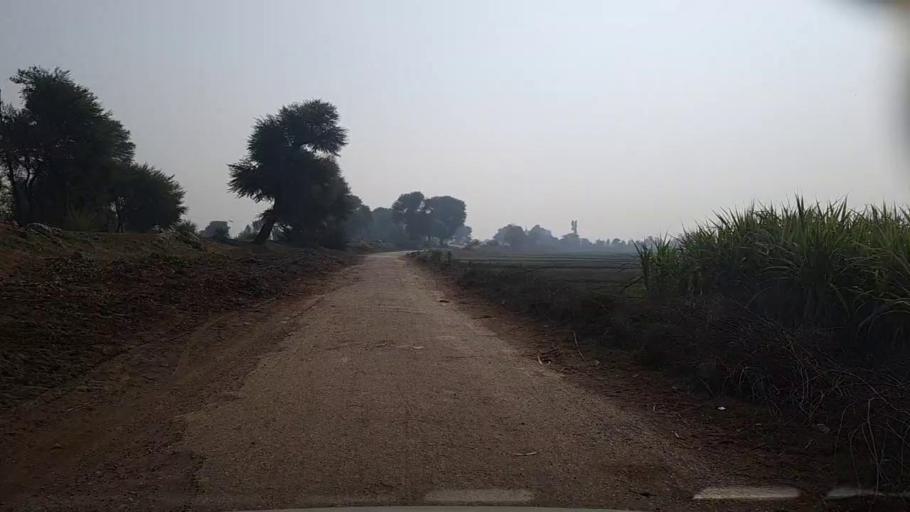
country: PK
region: Sindh
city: Setharja Old
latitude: 27.1329
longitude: 68.5117
